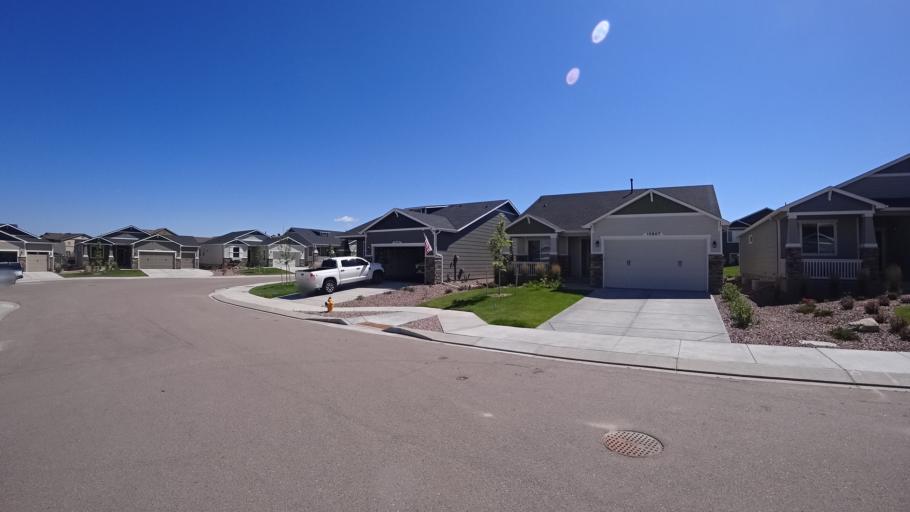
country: US
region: Colorado
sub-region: El Paso County
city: Black Forest
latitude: 38.9913
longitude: -104.7624
